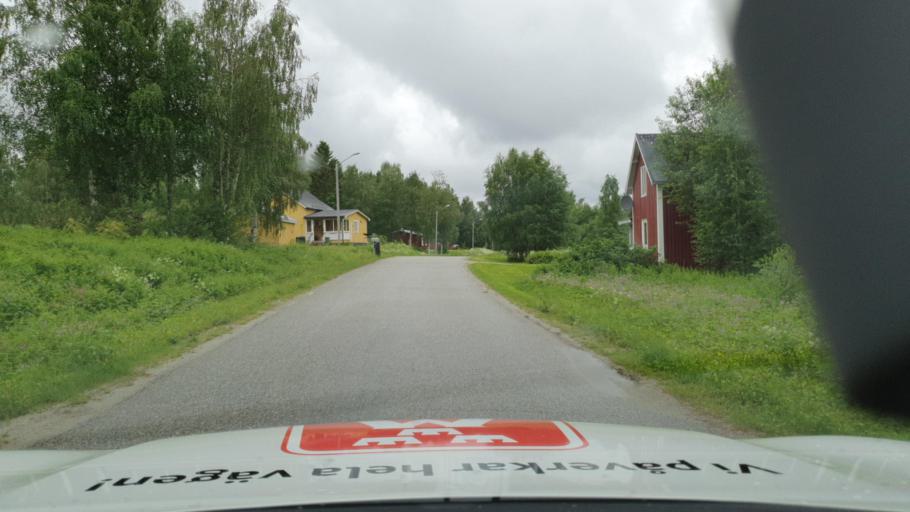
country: SE
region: Vaesterbotten
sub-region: Dorotea Kommun
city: Dorotea
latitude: 64.0977
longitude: 16.6473
